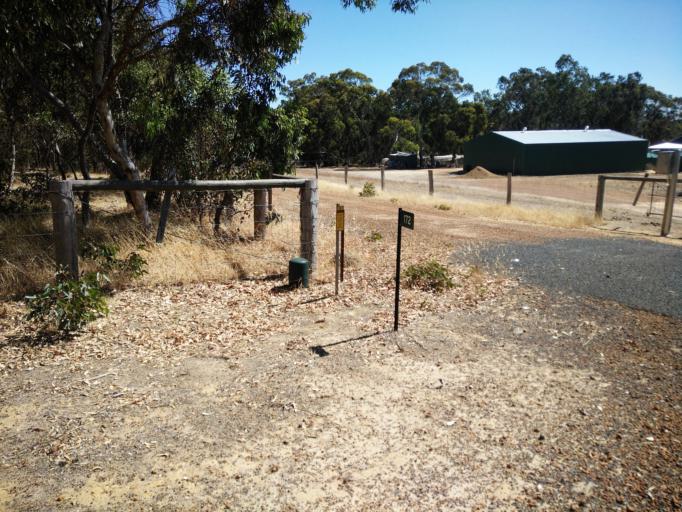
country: AU
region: Western Australia
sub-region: Boyup Brook
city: Boyup Brook
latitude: -33.8334
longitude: 116.3448
